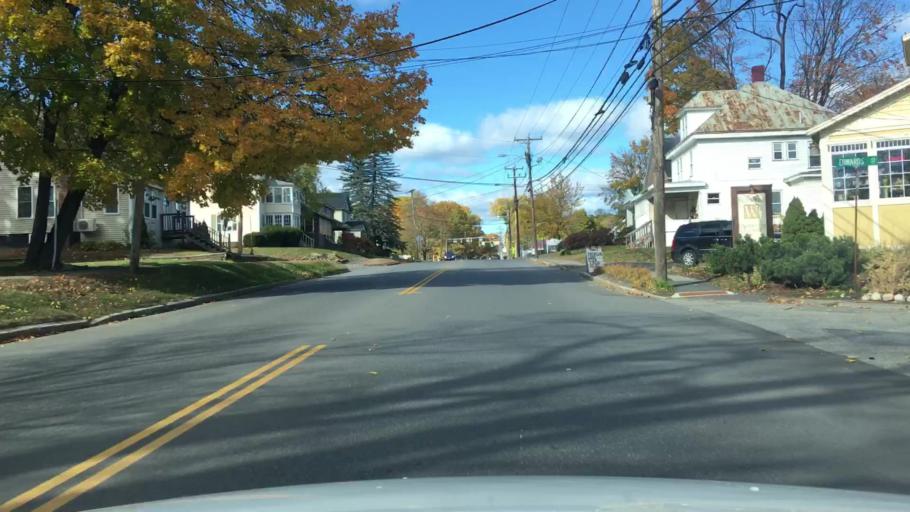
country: US
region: Maine
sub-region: Kennebec County
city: Waterville
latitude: 44.5607
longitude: -69.6342
